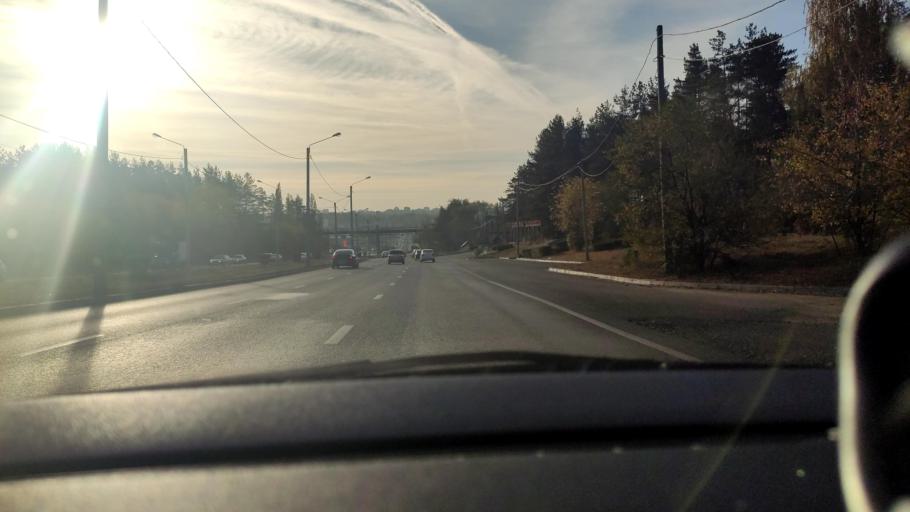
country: RU
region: Voronezj
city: Pridonskoy
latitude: 51.6740
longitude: 39.1170
